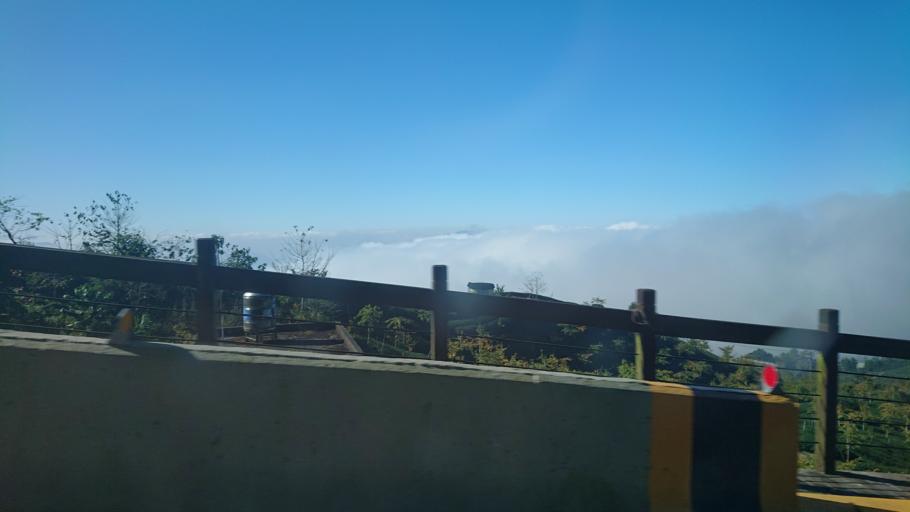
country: TW
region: Taiwan
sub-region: Chiayi
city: Jiayi Shi
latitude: 23.4791
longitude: 120.7001
